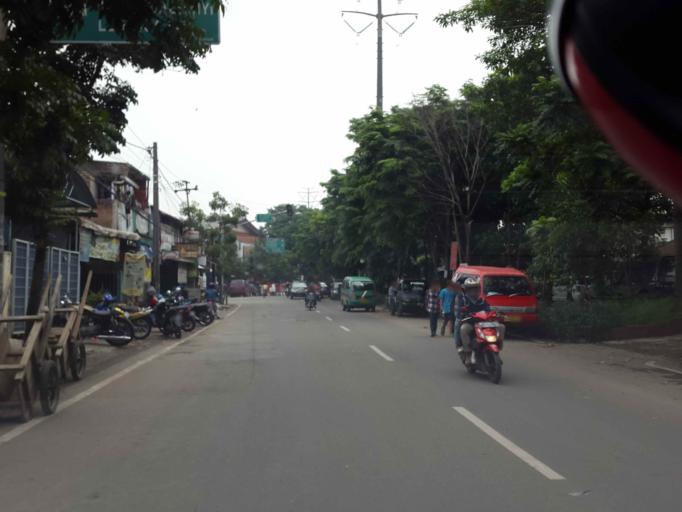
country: ID
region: West Java
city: Margahayukencana
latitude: -6.9205
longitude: 107.5631
